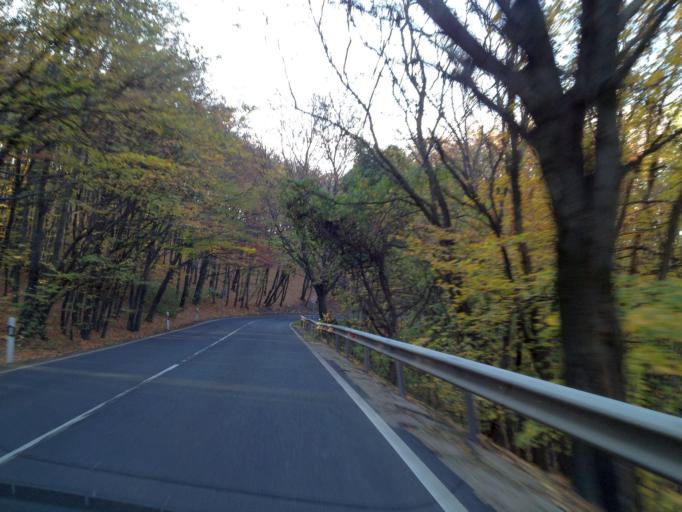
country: HU
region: Veszprem
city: Zirc
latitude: 47.3408
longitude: 17.8840
